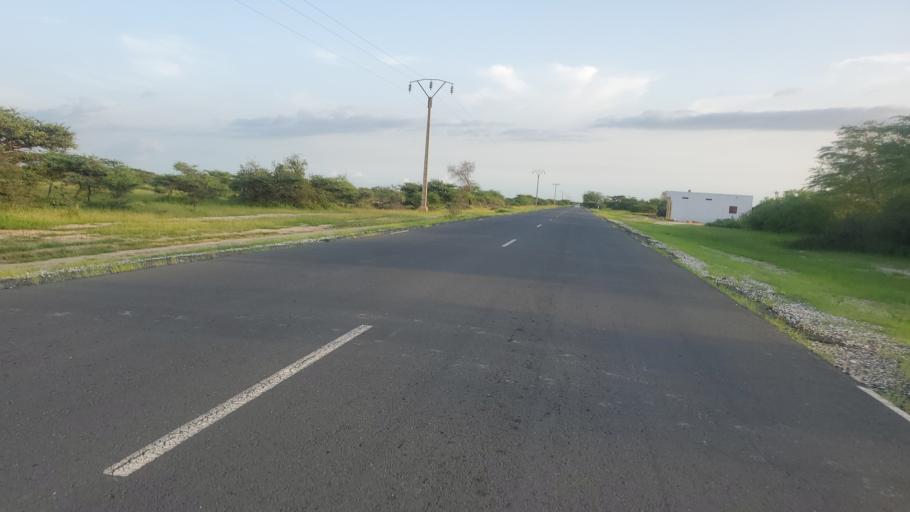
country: SN
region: Saint-Louis
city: Saint-Louis
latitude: 16.1818
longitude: -16.4095
